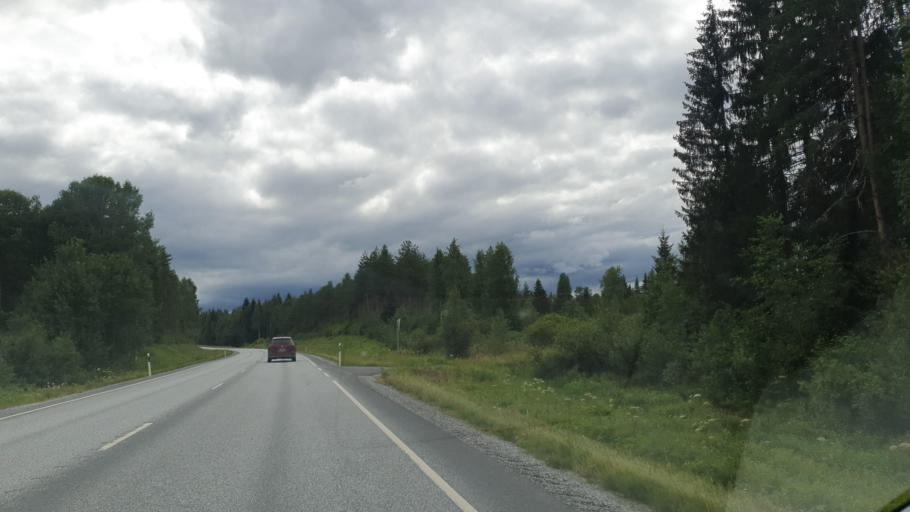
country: FI
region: Northern Savo
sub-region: Ylae-Savo
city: Sonkajaervi
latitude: 63.8383
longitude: 27.4260
